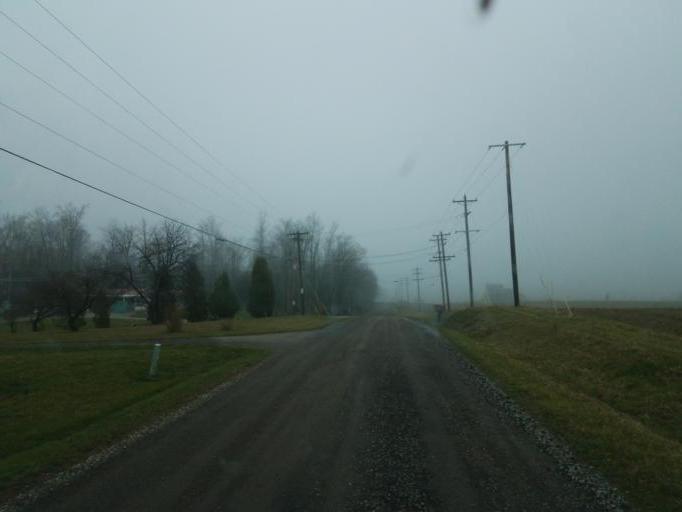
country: US
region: Ohio
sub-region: Richland County
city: Lexington
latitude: 40.6737
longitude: -82.6611
